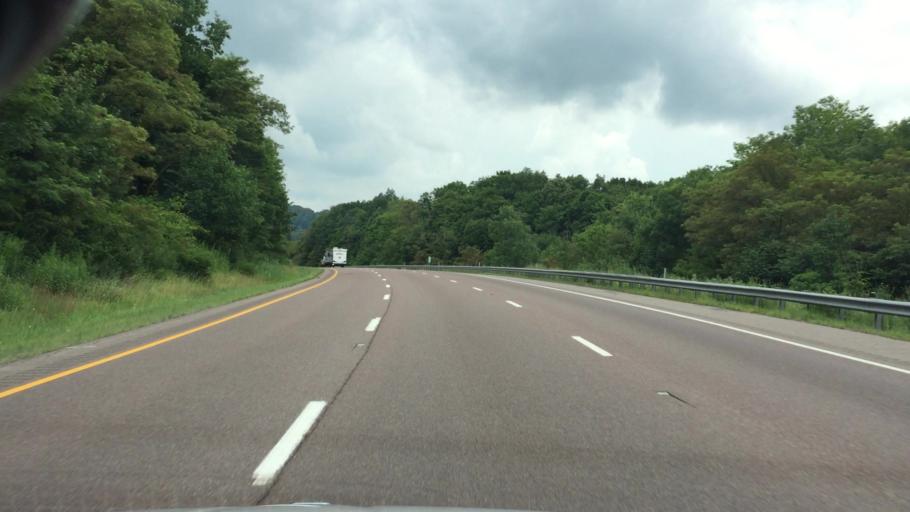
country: US
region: Maryland
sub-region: Allegany County
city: Frostburg
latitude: 39.6420
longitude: -78.8720
